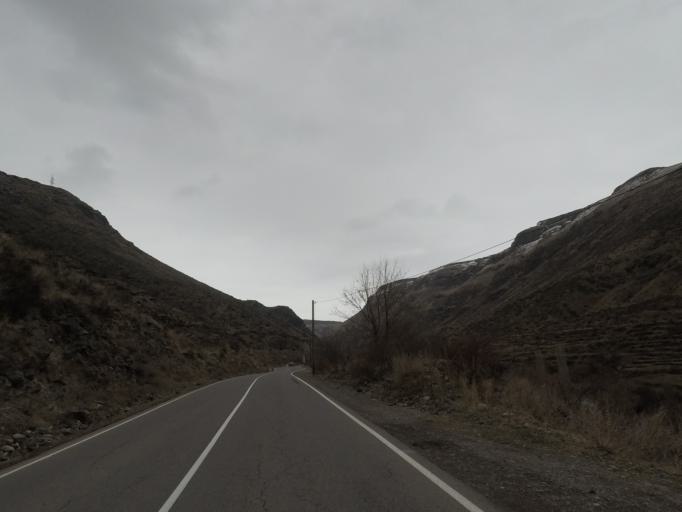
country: GE
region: Samtskhe-Javakheti
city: Aspindza
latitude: 41.4819
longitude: 43.2882
